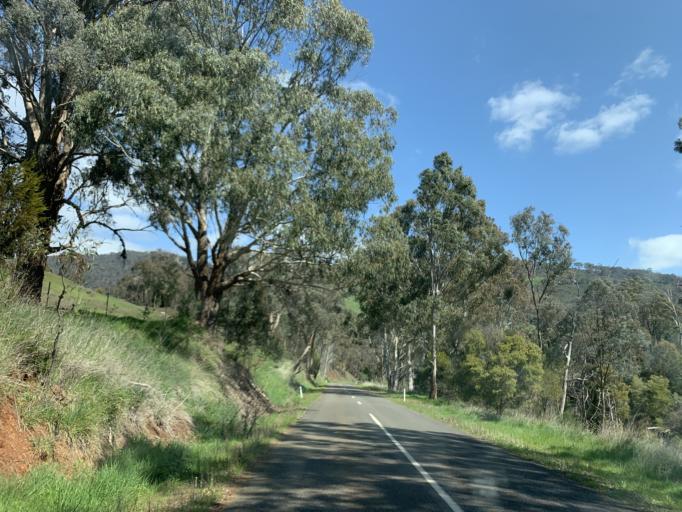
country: AU
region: Victoria
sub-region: Mansfield
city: Mansfield
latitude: -36.8277
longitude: 146.1278
